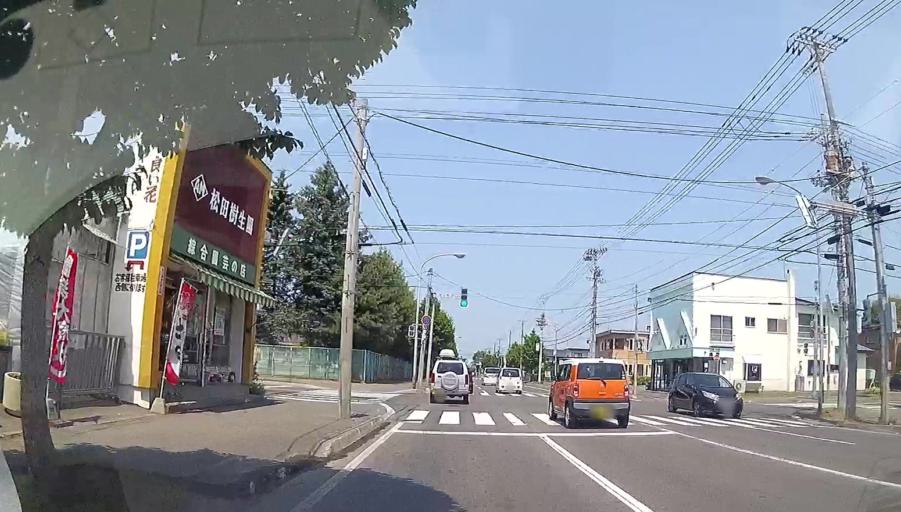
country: JP
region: Hokkaido
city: Obihiro
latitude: 42.9010
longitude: 143.2001
